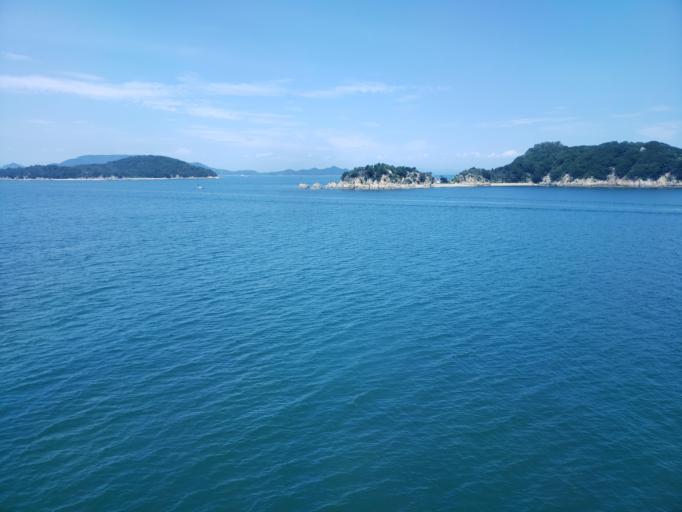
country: JP
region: Kagawa
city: Tonosho
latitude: 34.4051
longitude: 134.1351
